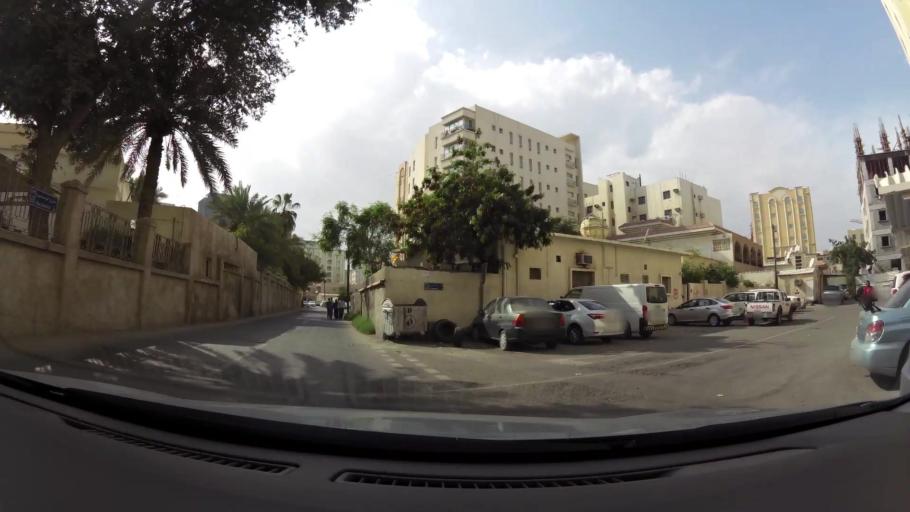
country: QA
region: Baladiyat ad Dawhah
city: Doha
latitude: 25.2810
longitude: 51.5128
